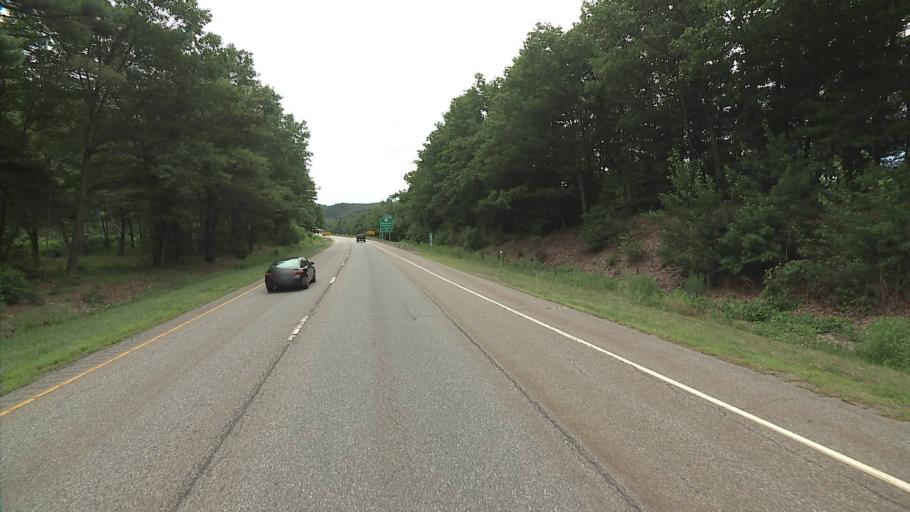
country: US
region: Connecticut
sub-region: Litchfield County
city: Torrington
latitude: 41.7742
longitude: -73.1148
